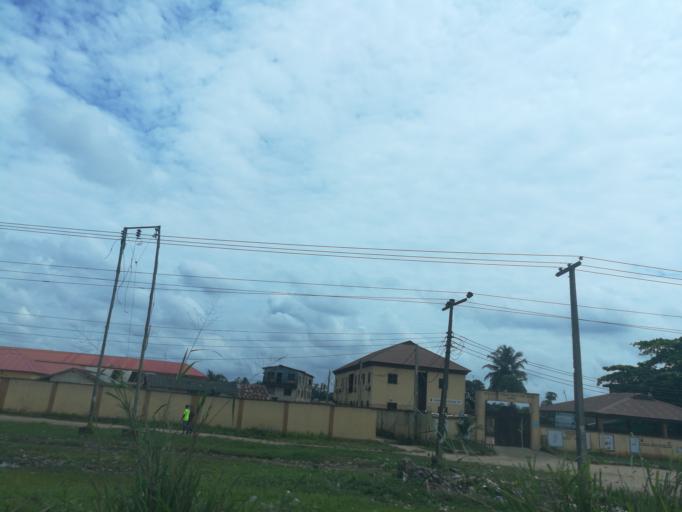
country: NG
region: Lagos
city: Ikotun
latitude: 6.4970
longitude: 3.1184
